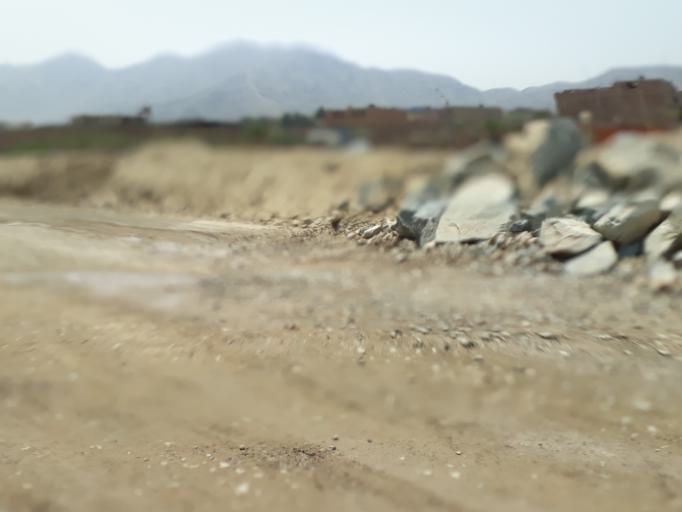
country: PE
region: Lima
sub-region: Lima
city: Santa Maria
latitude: -11.9927
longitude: -76.9073
